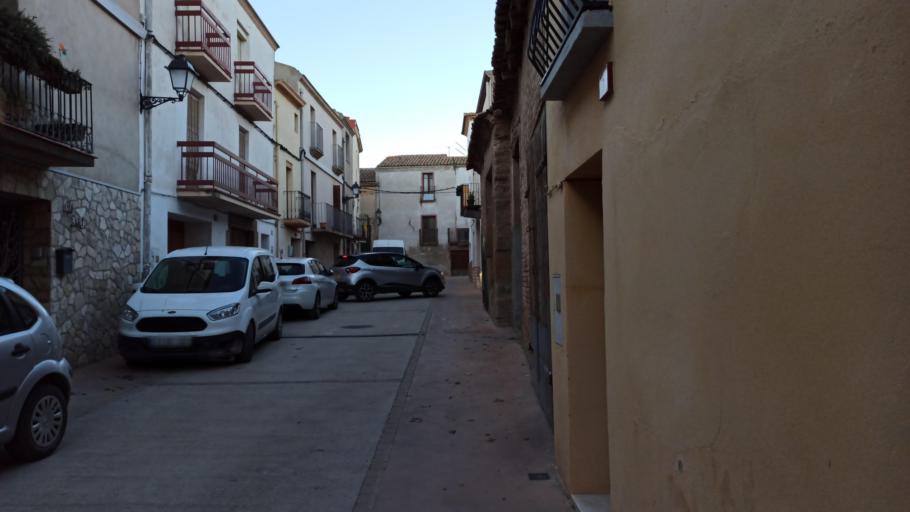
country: ES
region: Catalonia
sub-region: Provincia de Lleida
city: Penelles
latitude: 41.7571
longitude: 0.9637
